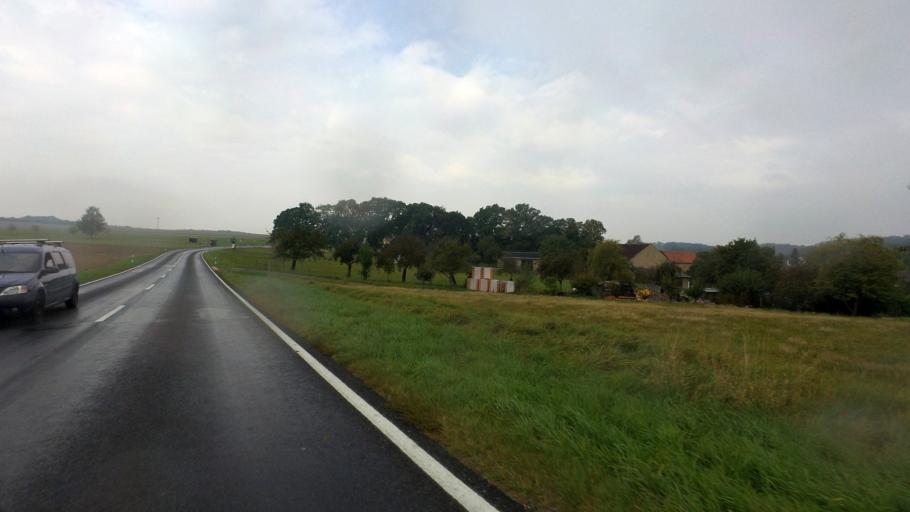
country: DE
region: Saxony
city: Arnsdorf
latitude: 51.1122
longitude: 13.9581
